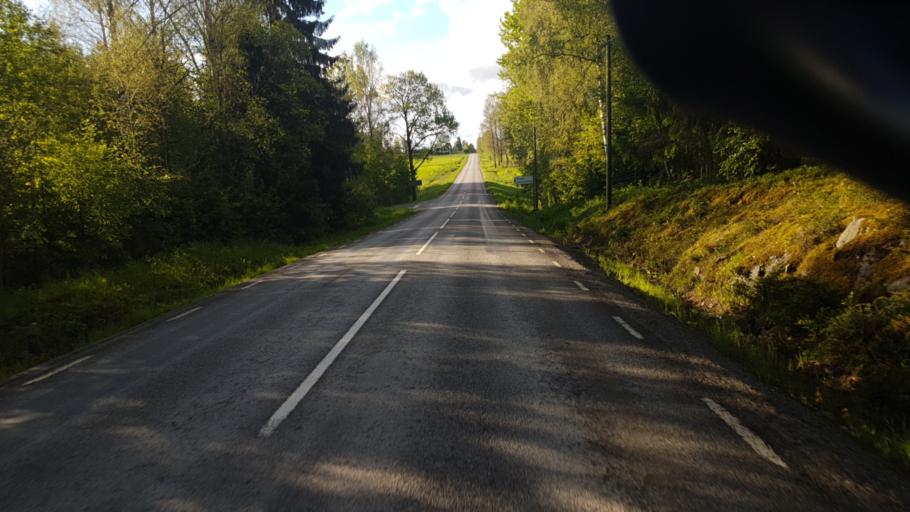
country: SE
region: Vaermland
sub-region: Arvika Kommun
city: Arvika
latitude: 59.6166
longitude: 12.5132
